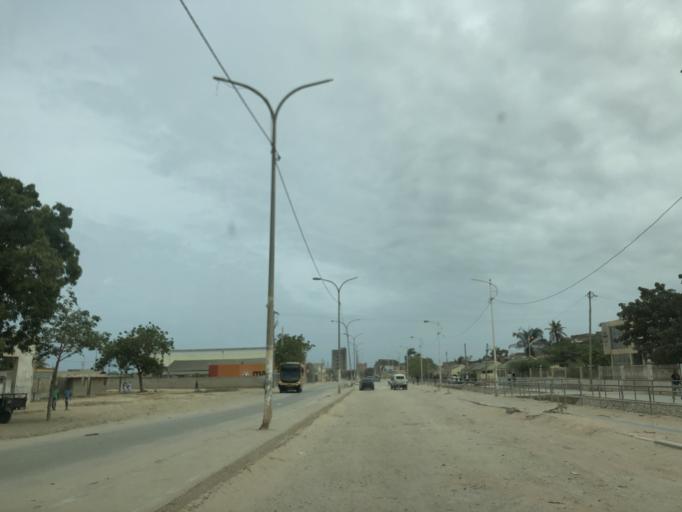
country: AO
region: Cuanza Sul
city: Sumbe
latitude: -11.2113
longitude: 13.8462
